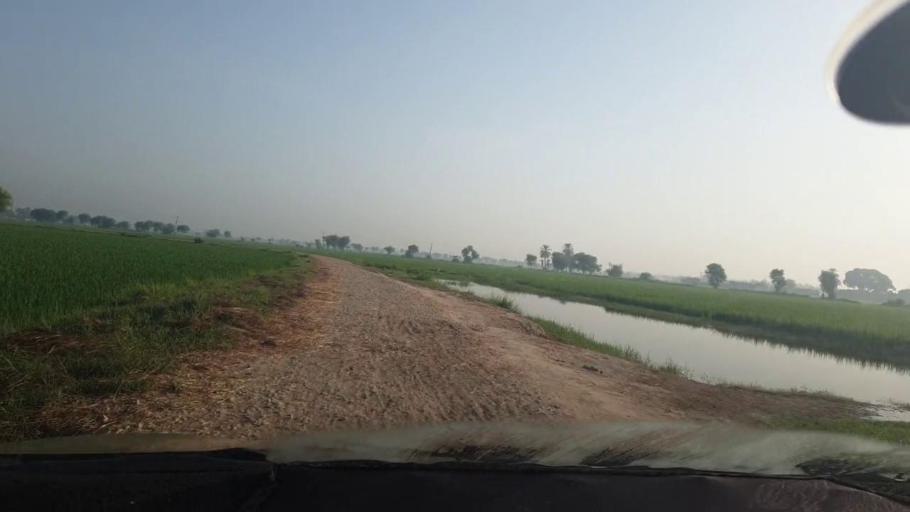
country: PK
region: Sindh
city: Kambar
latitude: 27.6268
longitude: 68.0183
